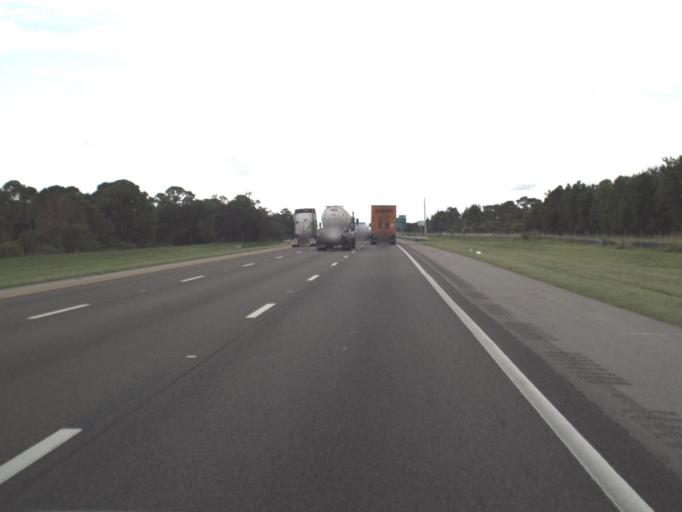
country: US
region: Florida
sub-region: Sarasota County
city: Nokomis
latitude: 27.1507
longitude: -82.4203
